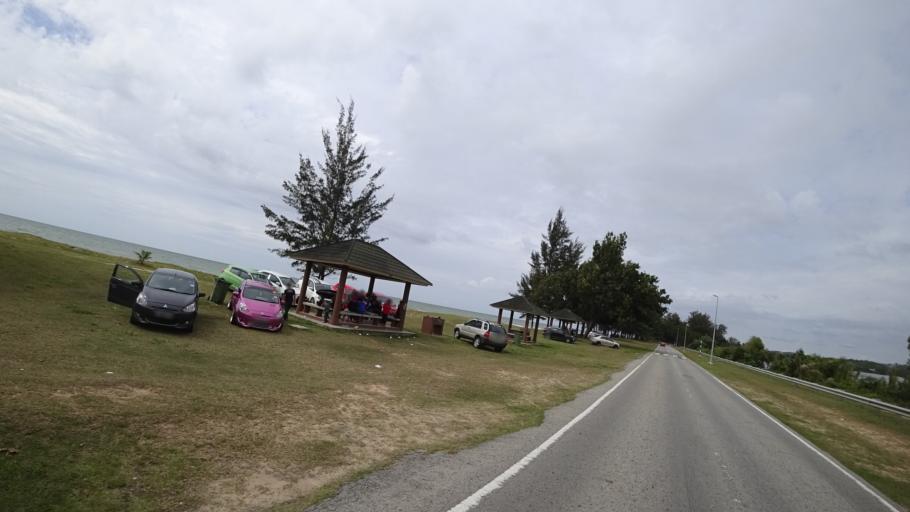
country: BN
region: Tutong
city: Tutong
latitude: 4.8038
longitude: 114.6336
